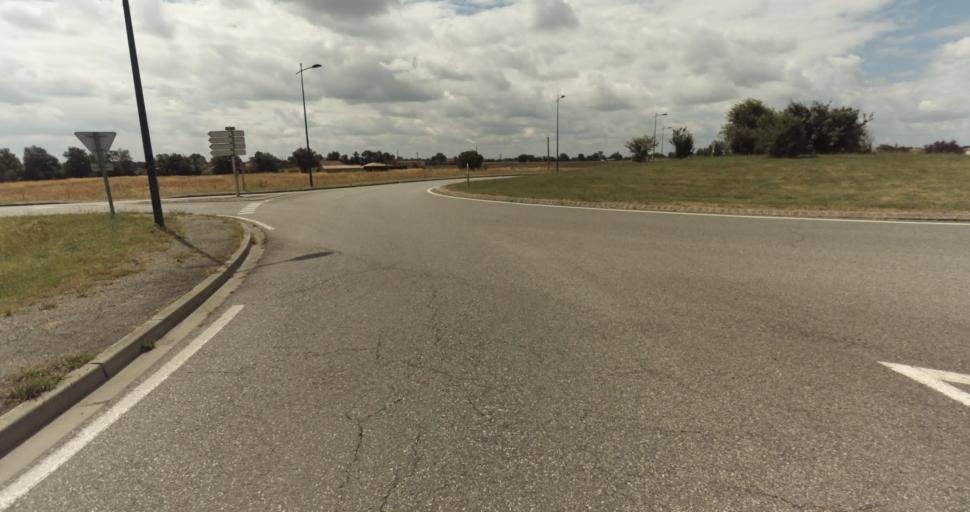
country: FR
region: Midi-Pyrenees
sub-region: Departement de la Haute-Garonne
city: Fontenilles
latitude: 43.5569
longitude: 1.1801
